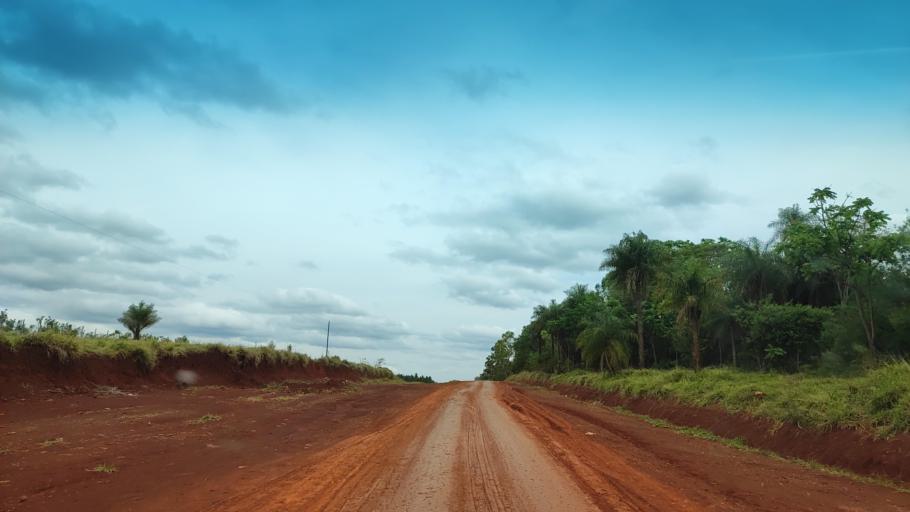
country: AR
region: Misiones
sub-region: Departamento de Capital
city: Posadas
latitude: -27.4849
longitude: -55.9708
